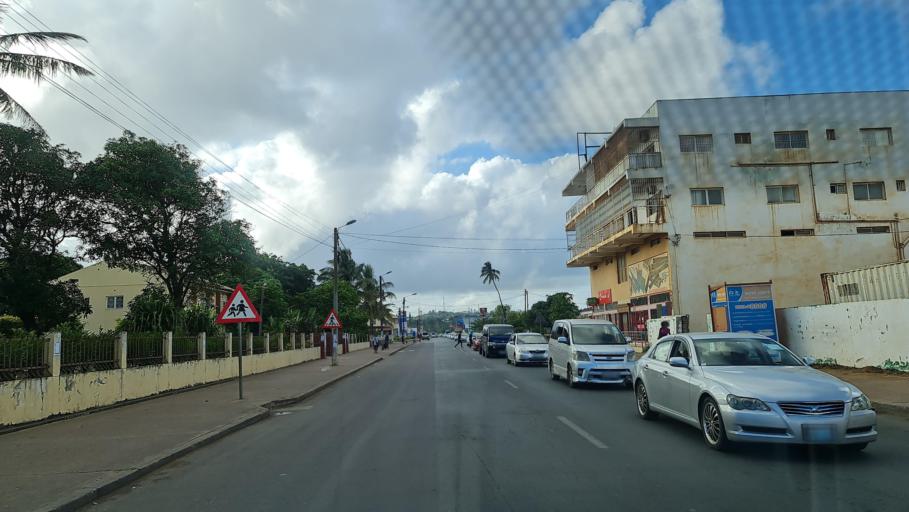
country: MZ
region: Gaza
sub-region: Xai-Xai District
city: Xai-Xai
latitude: -25.0466
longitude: 33.6444
